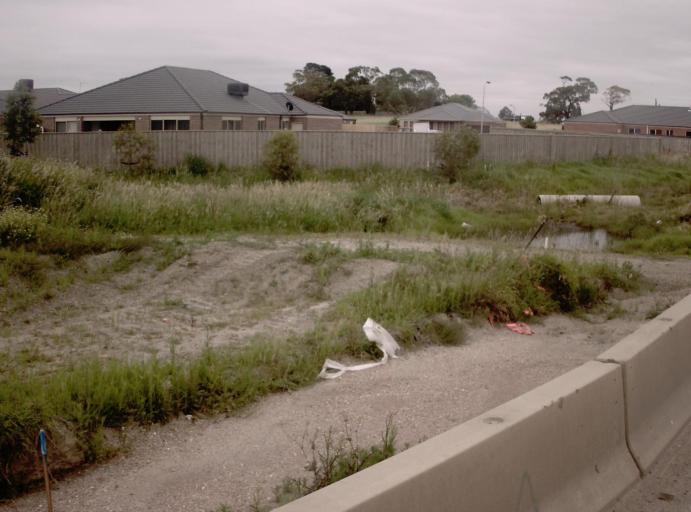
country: AU
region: Victoria
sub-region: Casey
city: Lynbrook
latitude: -38.0473
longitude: 145.2648
